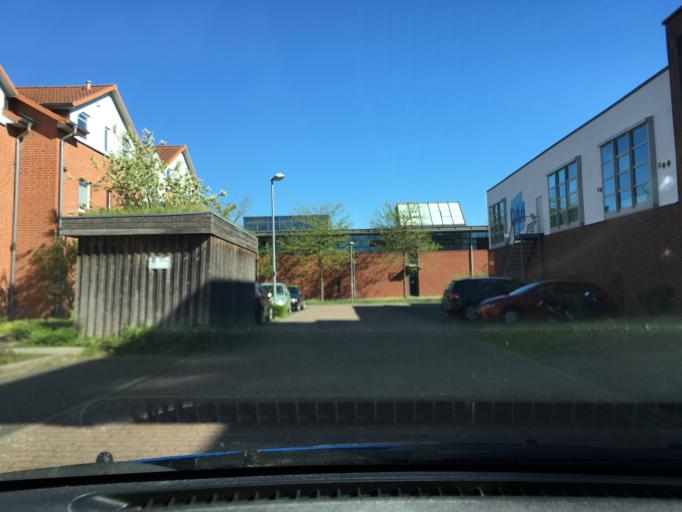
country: DE
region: Lower Saxony
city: Lueneburg
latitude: 53.2270
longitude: 10.4009
